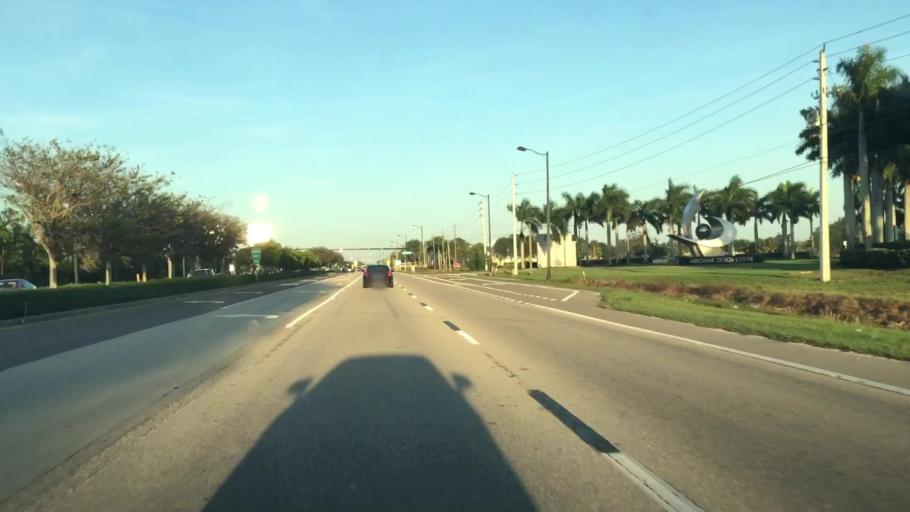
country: US
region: Florida
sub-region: Lee County
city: Estero
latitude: 26.4341
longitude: -81.7741
